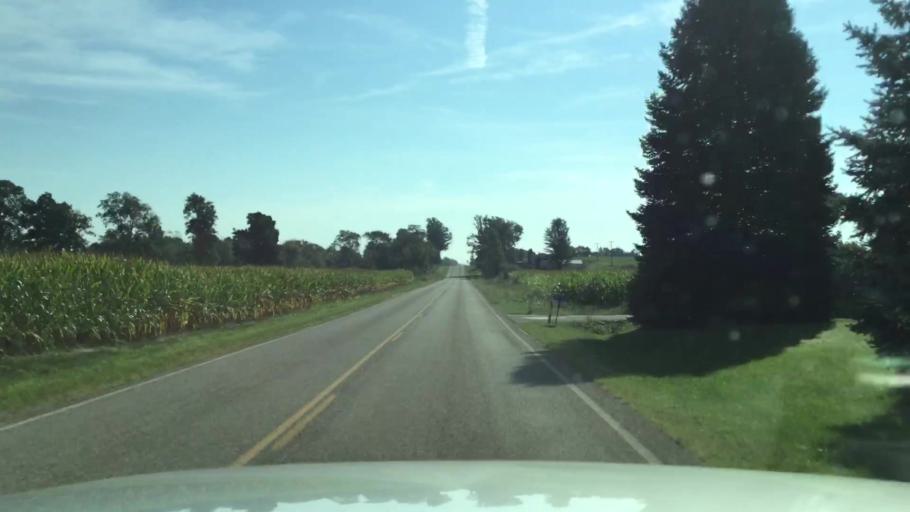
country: US
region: Michigan
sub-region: Lenawee County
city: Hudson
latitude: 41.9276
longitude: -84.3894
